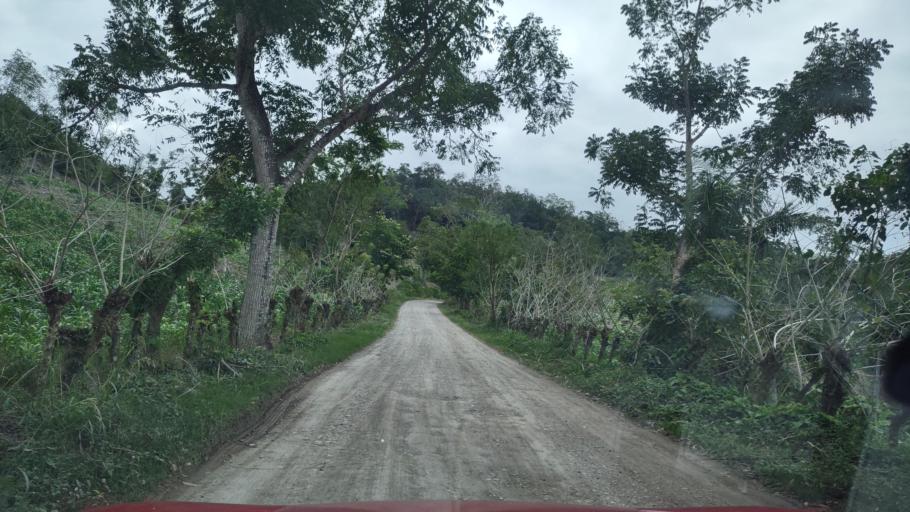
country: MX
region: Veracruz
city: Papantla de Olarte
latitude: 20.4210
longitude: -97.2724
